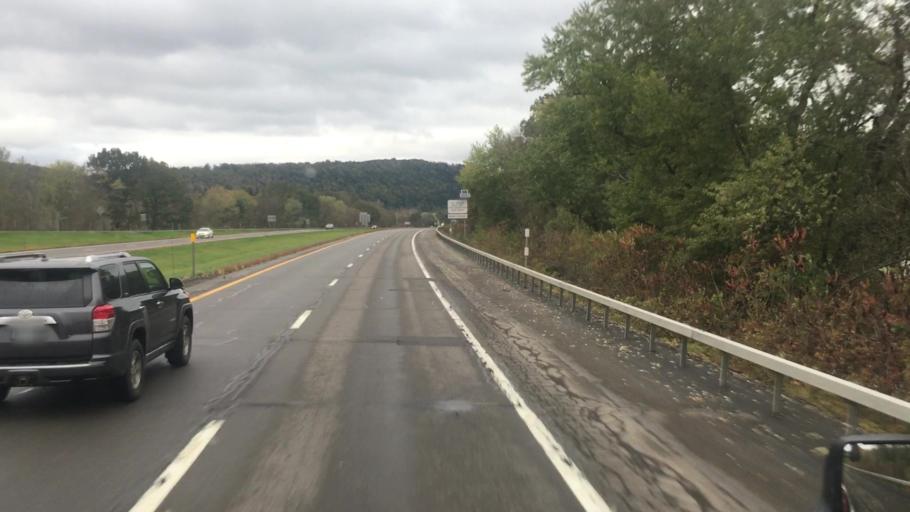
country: US
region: New York
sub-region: Tioga County
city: Owego
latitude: 42.0959
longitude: -76.2637
